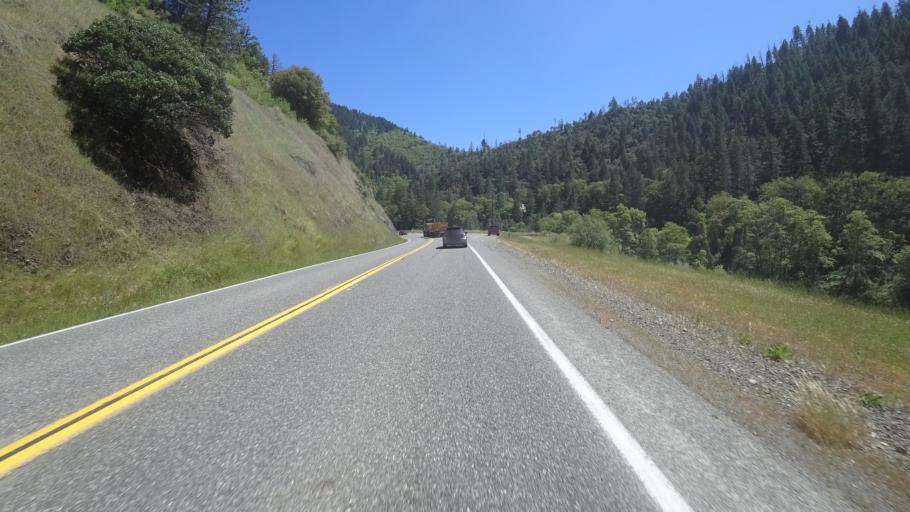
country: US
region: California
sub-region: Trinity County
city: Hayfork
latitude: 40.7623
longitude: -123.2886
